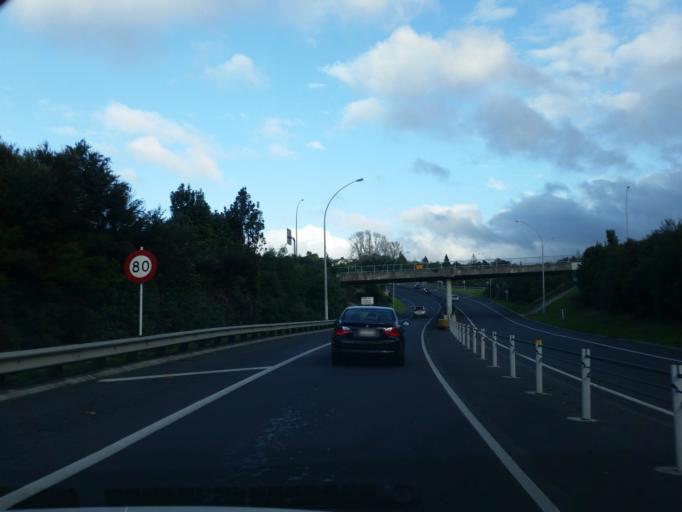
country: NZ
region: Bay of Plenty
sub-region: Tauranga City
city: Tauranga
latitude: -37.6962
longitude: 176.1268
